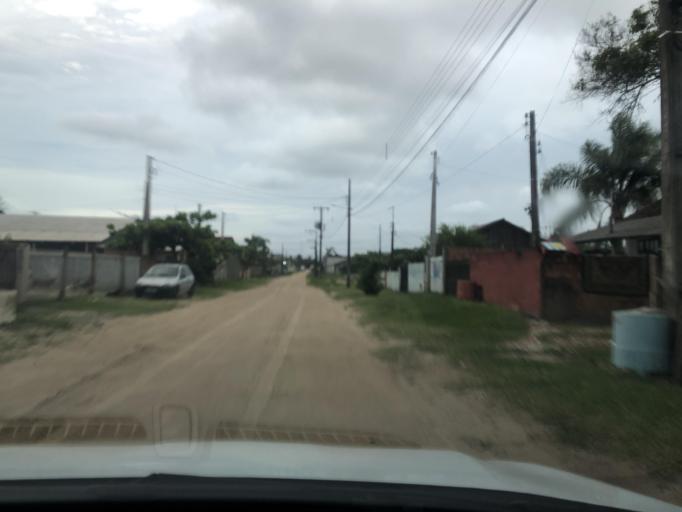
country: BR
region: Santa Catarina
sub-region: Sao Francisco Do Sul
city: Sao Francisco do Sul
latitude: -26.2356
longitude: -48.5222
